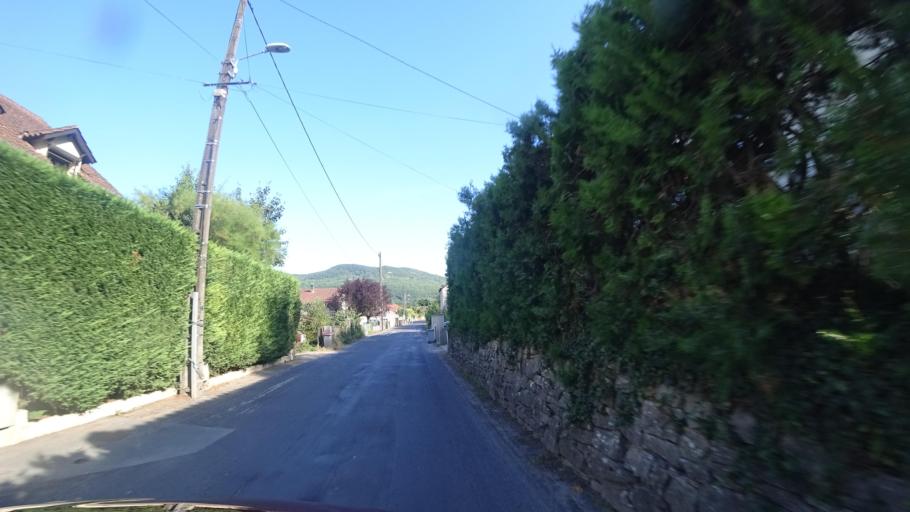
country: FR
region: Midi-Pyrenees
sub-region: Departement de l'Aveyron
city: Saint-Affrique
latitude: 43.9523
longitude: 2.8893
